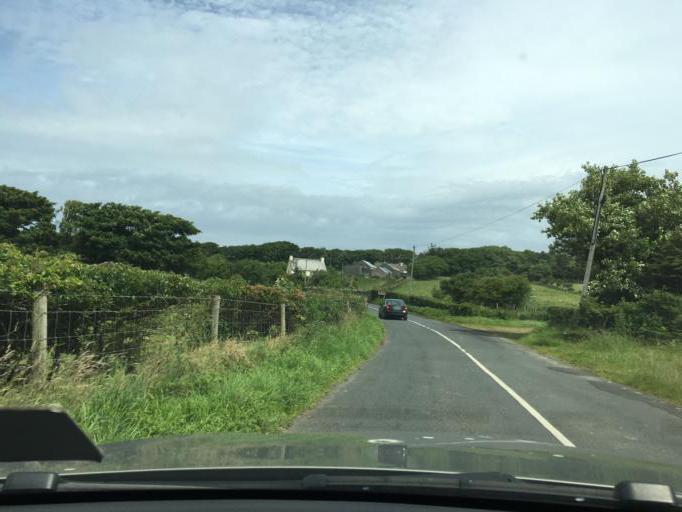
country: IE
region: Ulster
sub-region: County Donegal
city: Carndonagh
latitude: 55.3444
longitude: -7.3171
